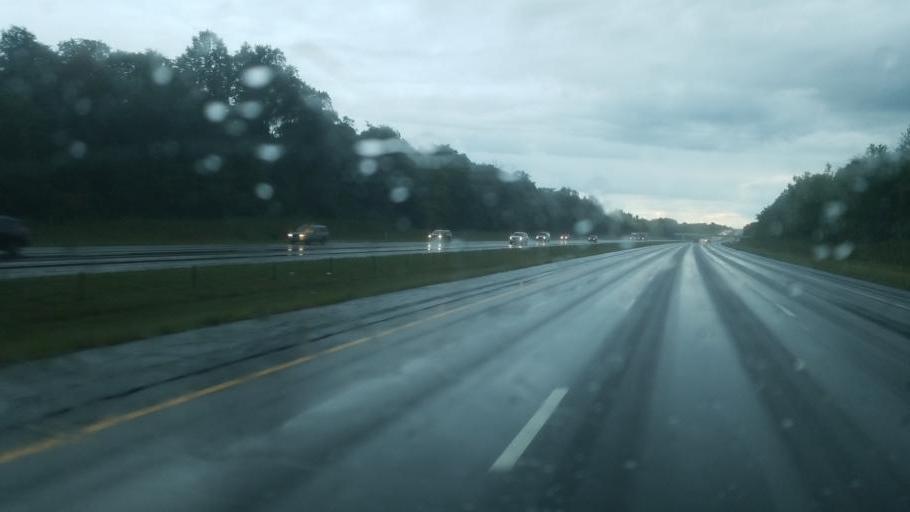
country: US
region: Ohio
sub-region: Medina County
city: Seville
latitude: 41.0684
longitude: -81.8475
